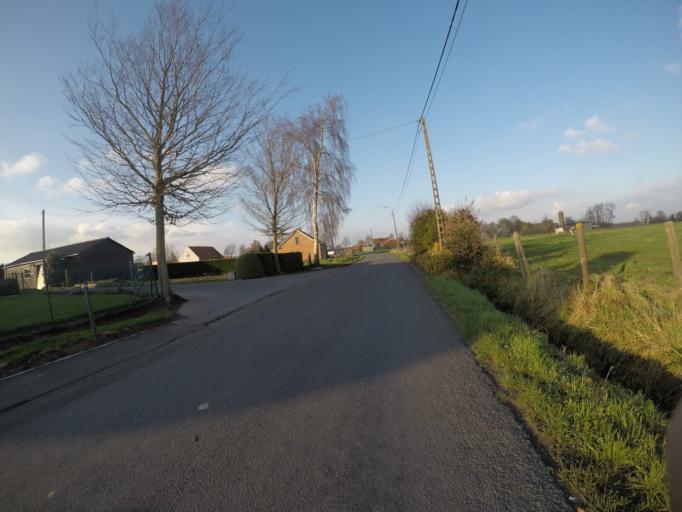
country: BE
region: Flanders
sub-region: Provincie West-Vlaanderen
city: Lichtervelde
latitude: 51.0484
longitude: 3.1789
